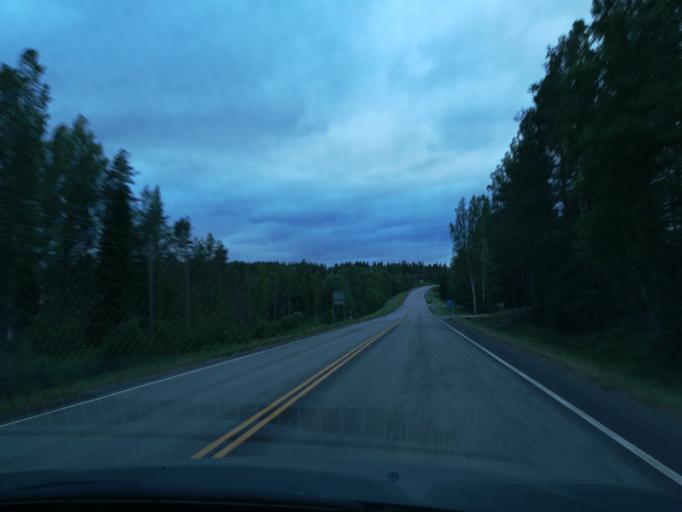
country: FI
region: Southern Savonia
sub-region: Mikkeli
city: Ristiina
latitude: 61.4570
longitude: 27.2596
